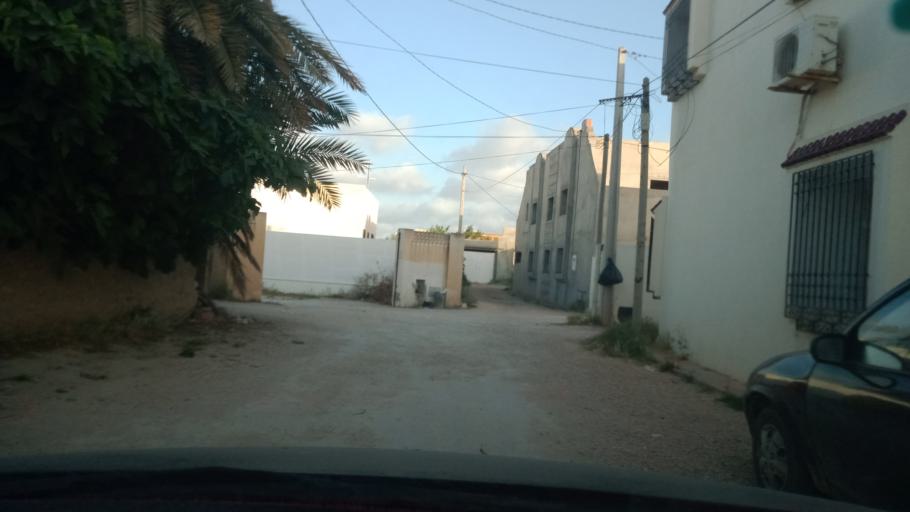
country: TN
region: Safaqis
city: Al Qarmadah
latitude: 34.8167
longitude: 10.7494
